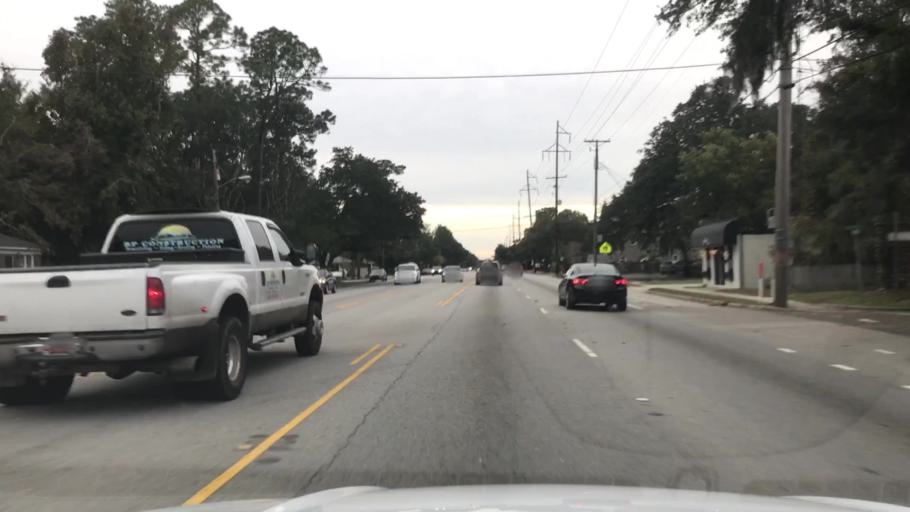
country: US
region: South Carolina
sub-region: Charleston County
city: Charleston
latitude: 32.7862
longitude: -79.9803
